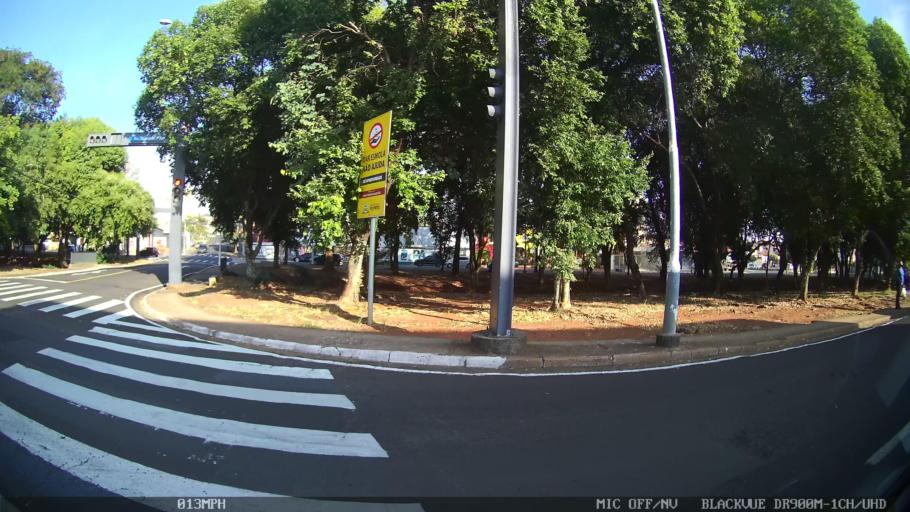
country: BR
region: Sao Paulo
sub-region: Sao Jose Do Rio Preto
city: Sao Jose do Rio Preto
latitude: -20.8191
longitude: -49.3656
